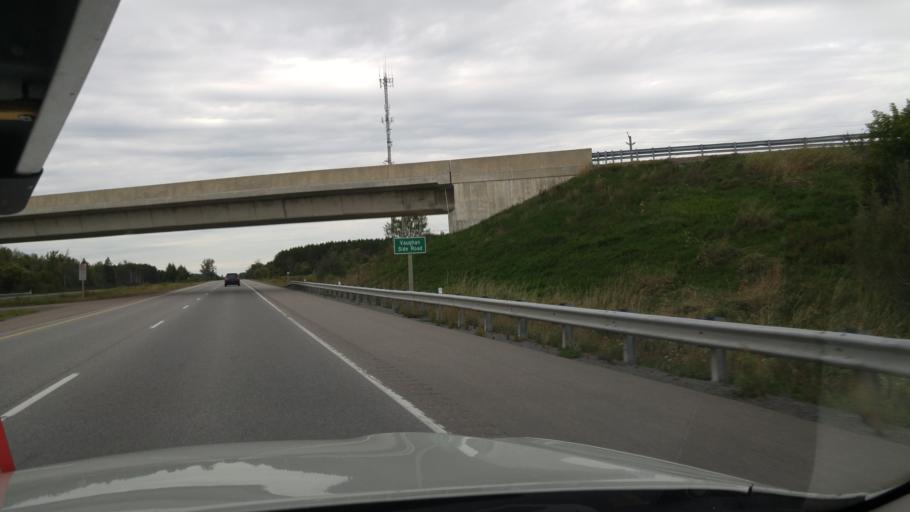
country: CA
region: Ontario
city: Carleton Place
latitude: 45.3214
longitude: -76.1000
